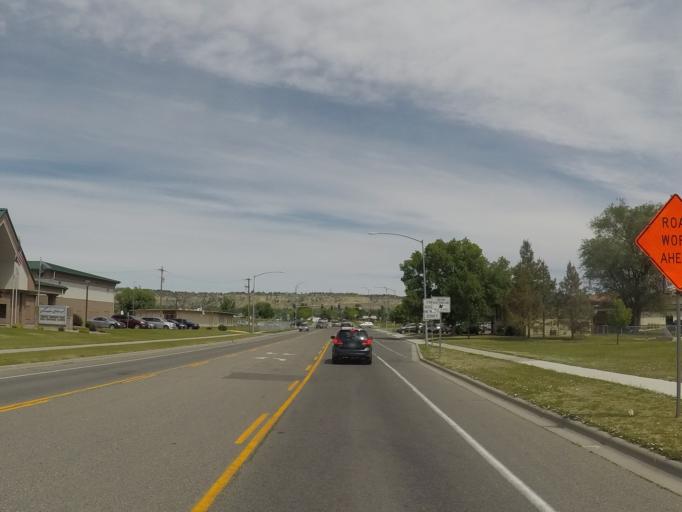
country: US
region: Montana
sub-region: Yellowstone County
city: Billings
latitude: 45.7752
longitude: -108.5969
